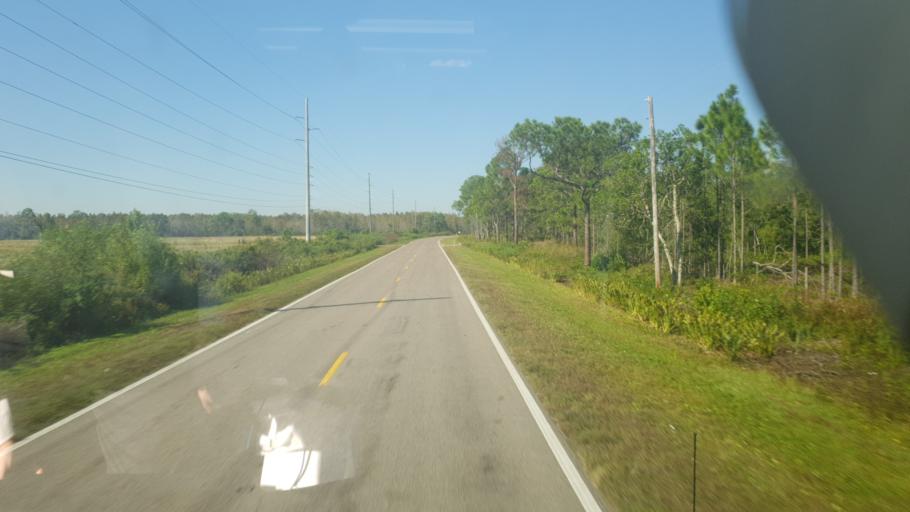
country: US
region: Florida
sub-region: Lake County
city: Four Corners
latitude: 28.3698
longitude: -81.7197
